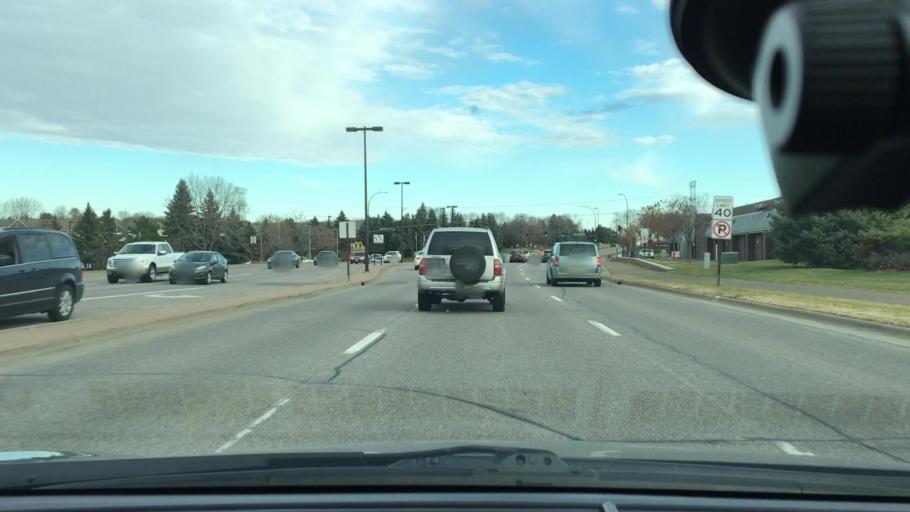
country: US
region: Minnesota
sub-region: Hennepin County
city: Maple Grove
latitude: 45.1049
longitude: -93.4540
